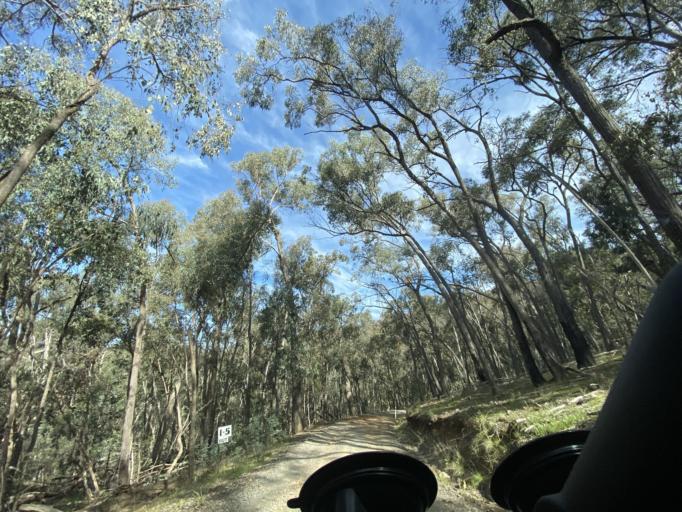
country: AU
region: Victoria
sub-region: Mansfield
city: Mansfield
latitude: -36.8003
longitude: 146.1163
